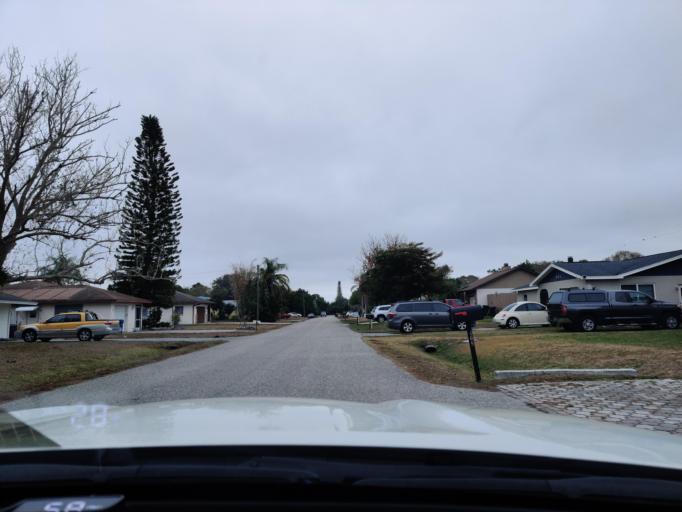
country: US
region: Florida
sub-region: Sarasota County
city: South Venice
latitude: 27.0387
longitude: -82.4053
